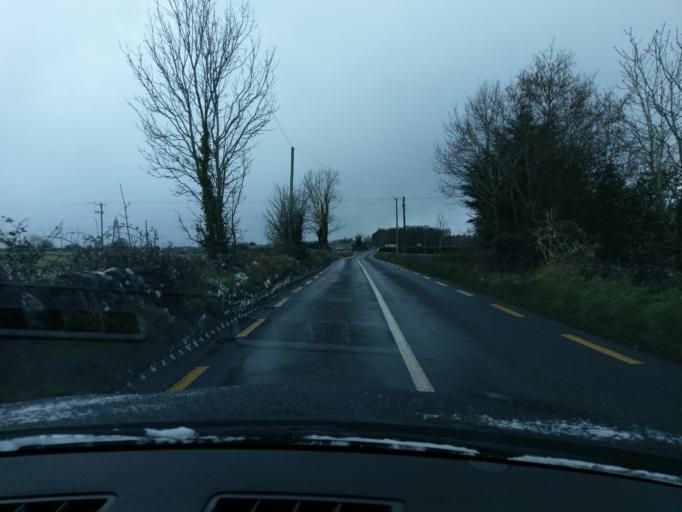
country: IE
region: Connaught
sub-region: County Galway
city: Athenry
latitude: 53.2861
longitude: -8.7810
